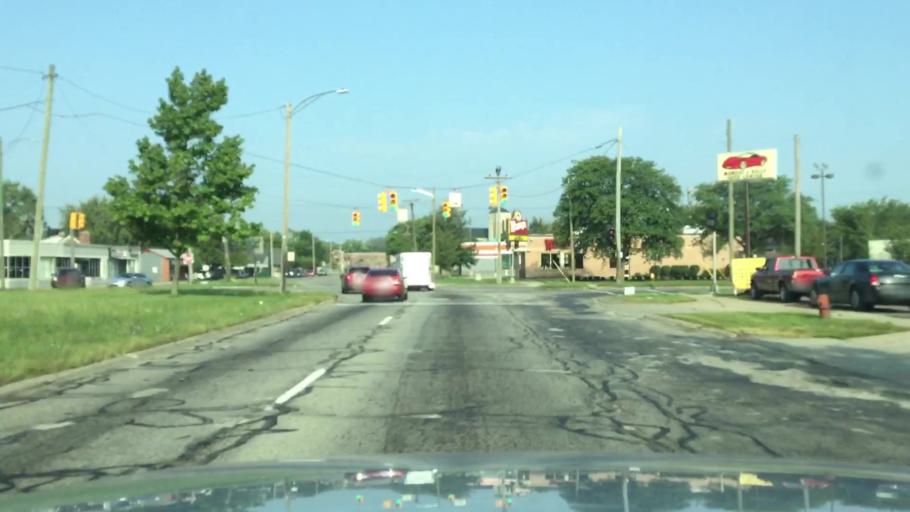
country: US
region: Michigan
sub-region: Wayne County
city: Harper Woods
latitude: 42.4345
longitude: -82.9523
